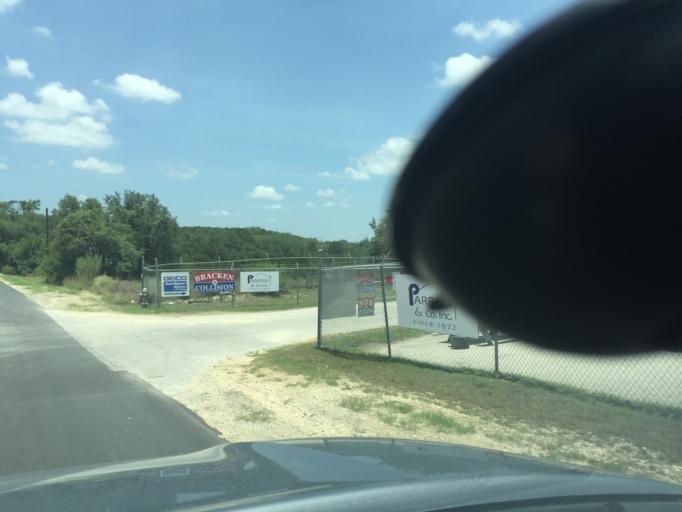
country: US
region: Texas
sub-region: Bexar County
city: Timberwood Park
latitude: 29.7002
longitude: -98.4543
